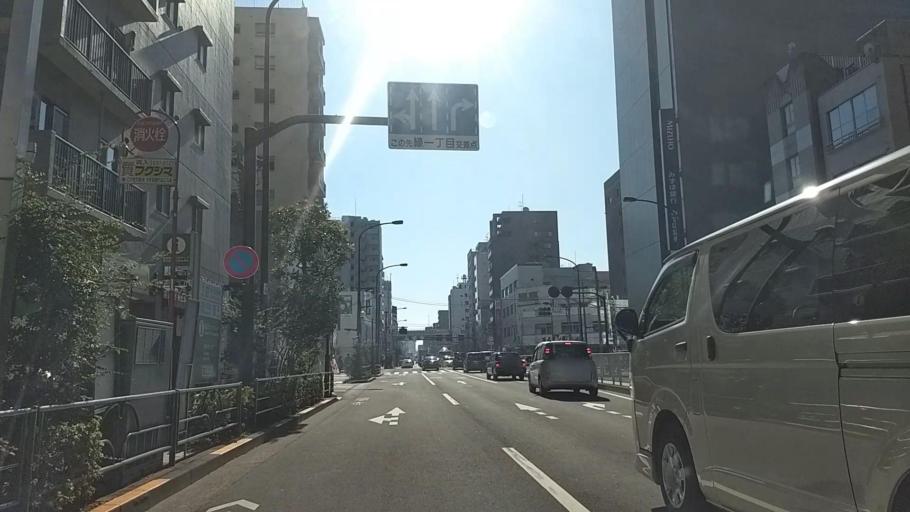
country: JP
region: Tokyo
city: Urayasu
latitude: 35.6952
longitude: 139.7976
